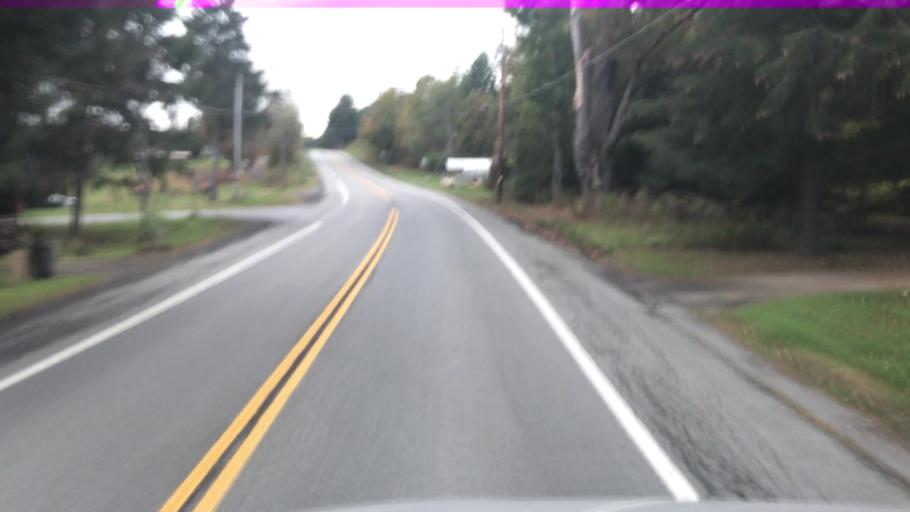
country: US
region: New York
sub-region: Otsego County
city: West End
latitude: 42.5301
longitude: -75.1728
